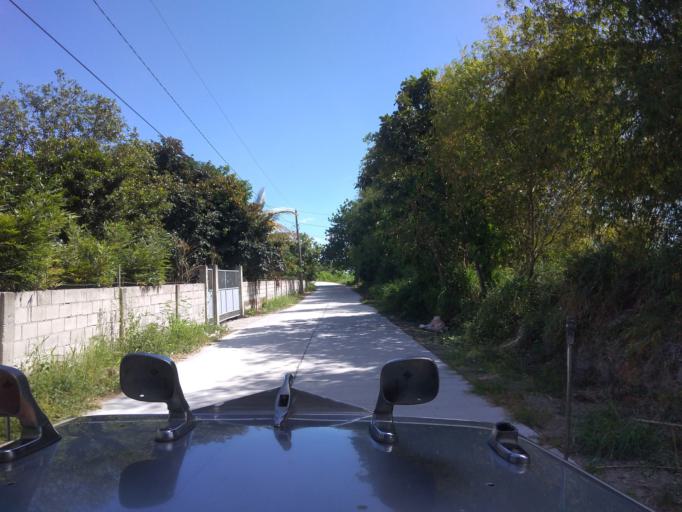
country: PH
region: Central Luzon
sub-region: Province of Pampanga
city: Bacolor
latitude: 15.0129
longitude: 120.6558
